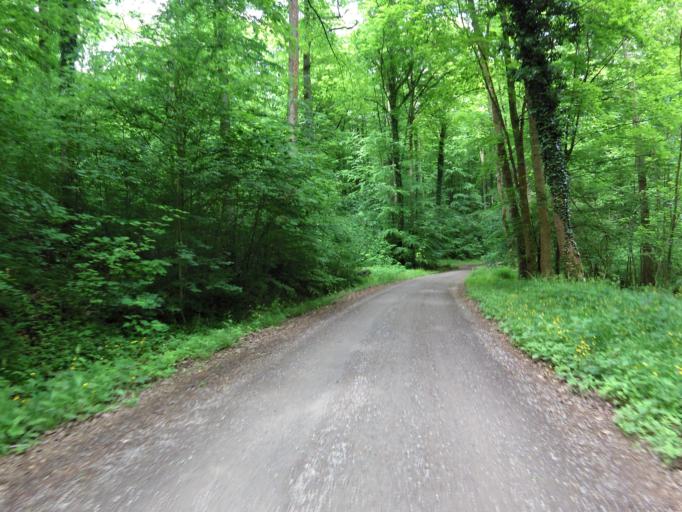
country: DE
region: Bavaria
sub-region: Regierungsbezirk Unterfranken
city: Wuerzburg
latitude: 49.7584
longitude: 9.8852
